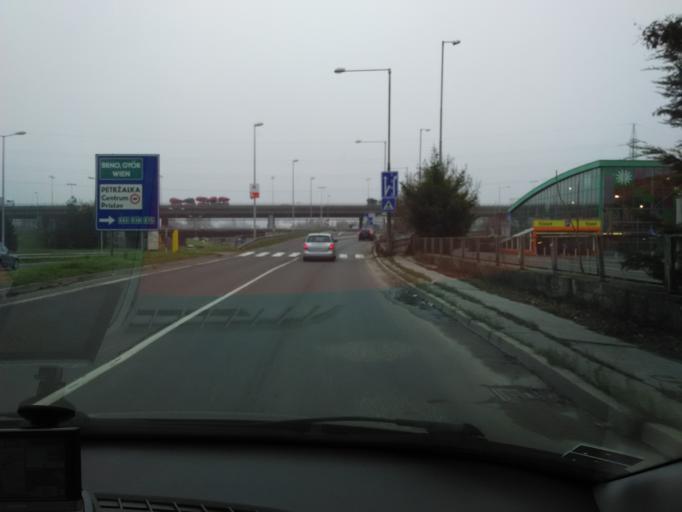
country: SK
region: Bratislavsky
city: Bratislava
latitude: 48.1438
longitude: 17.1515
